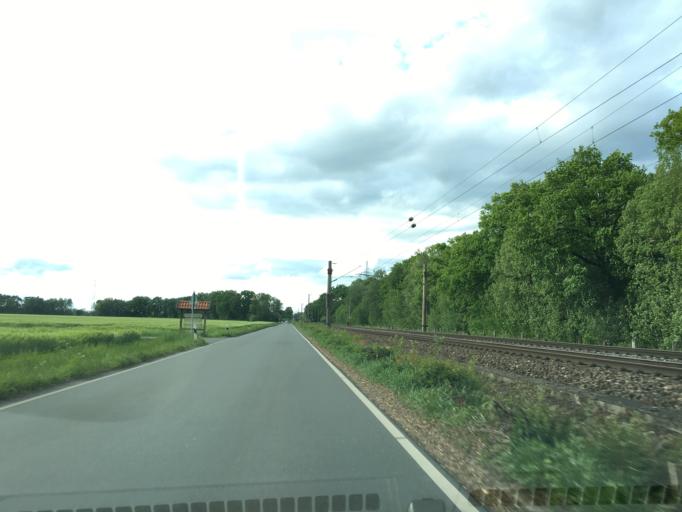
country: DE
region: North Rhine-Westphalia
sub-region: Regierungsbezirk Munster
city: Muenster
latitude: 52.0040
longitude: 7.6349
